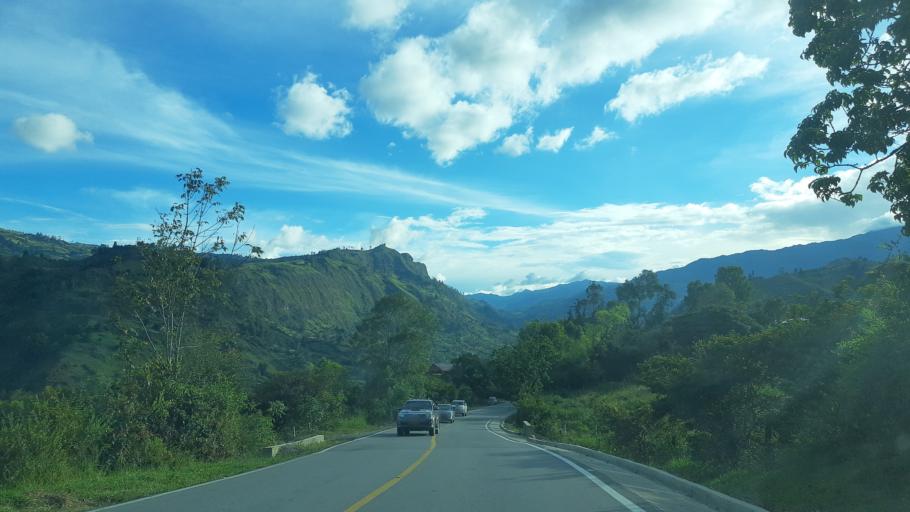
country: CO
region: Cundinamarca
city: Macheta
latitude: 5.0772
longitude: -73.5948
